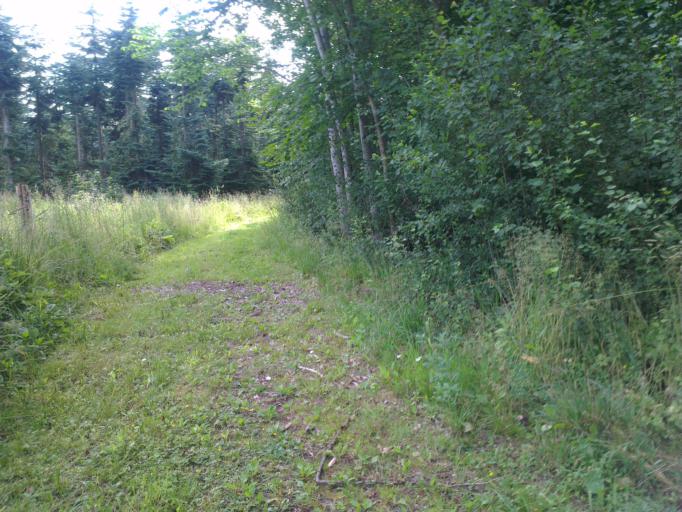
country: DK
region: Capital Region
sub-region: Frederikssund Kommune
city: Jaegerspris
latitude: 55.8848
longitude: 11.9822
